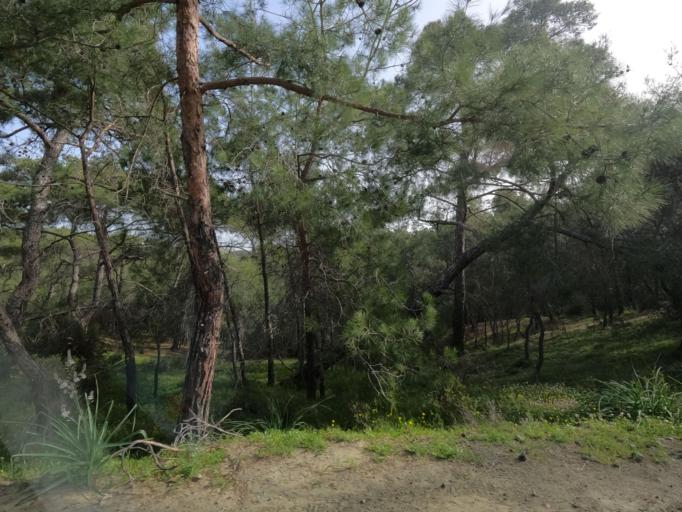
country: CY
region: Pafos
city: Polis
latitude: 34.9971
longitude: 32.3422
